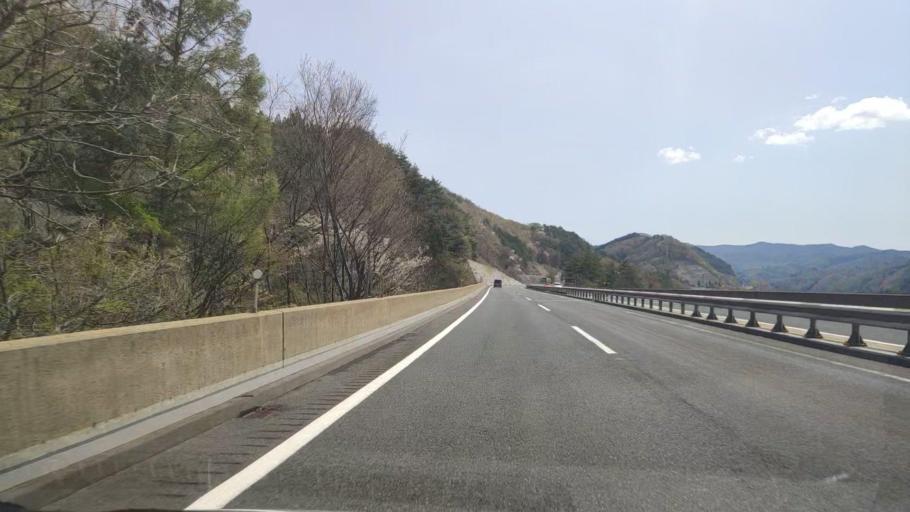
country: JP
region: Iwate
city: Ichinohe
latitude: 40.2298
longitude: 141.3168
